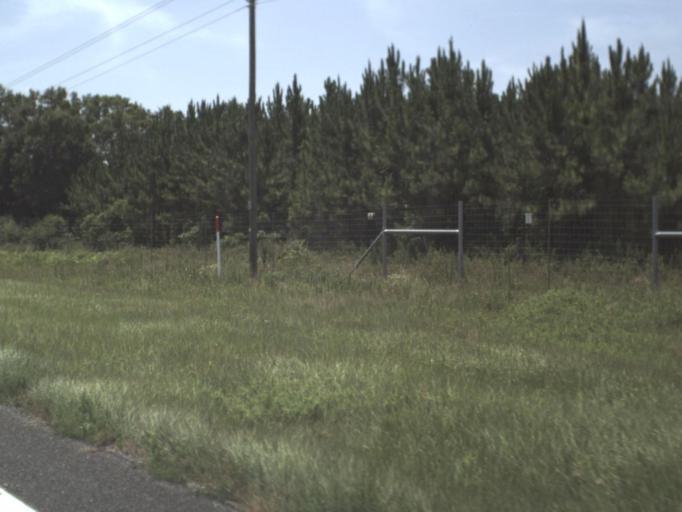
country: US
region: Florida
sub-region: Taylor County
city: Steinhatchee
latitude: 29.7864
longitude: -83.3309
